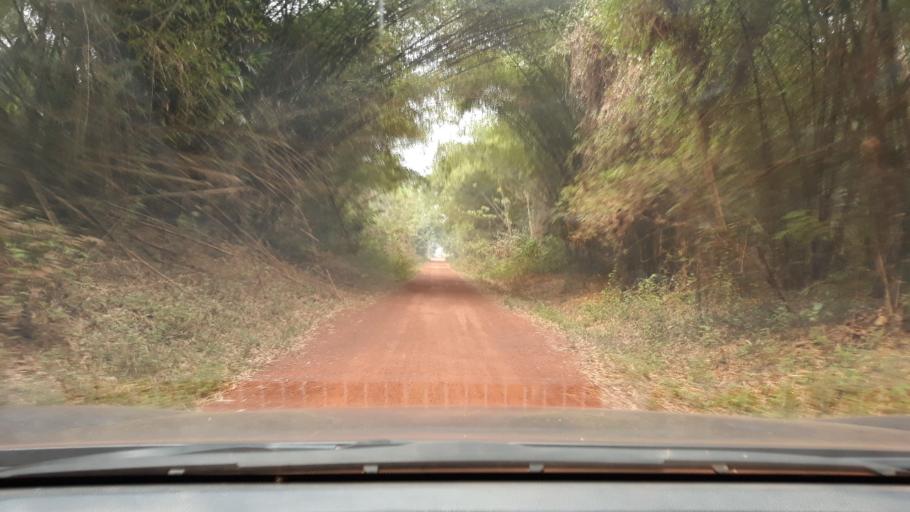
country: CD
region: Eastern Province
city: Aketi
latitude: 2.9357
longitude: 24.0969
